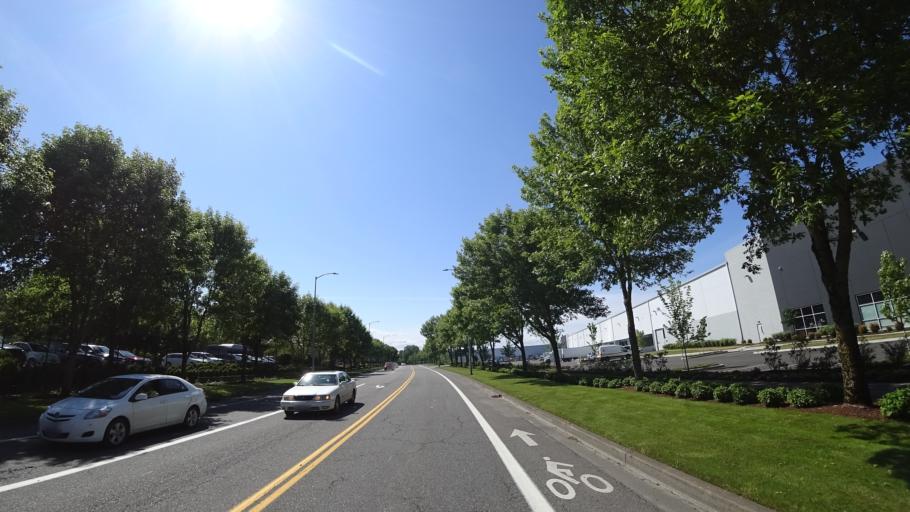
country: US
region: Oregon
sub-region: Multnomah County
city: Lents
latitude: 45.5692
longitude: -122.5607
